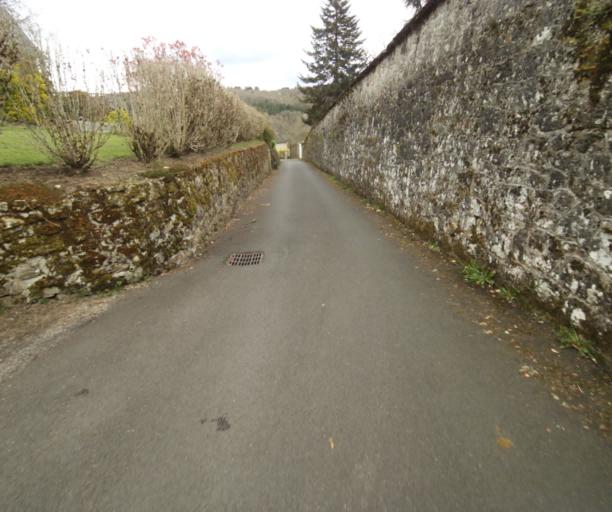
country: FR
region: Limousin
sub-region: Departement de la Correze
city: Argentat
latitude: 45.1958
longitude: 1.9721
